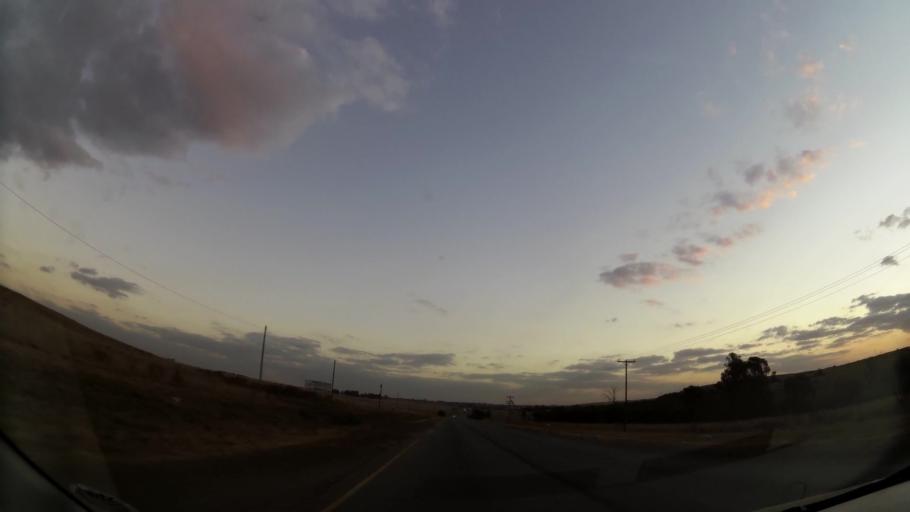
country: ZA
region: Gauteng
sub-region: West Rand District Municipality
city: Krugersdorp
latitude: -26.0490
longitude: 27.7135
